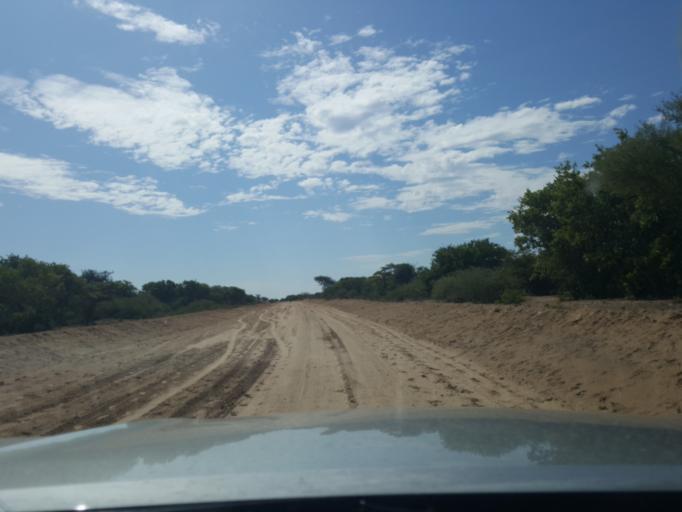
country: BW
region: Kweneng
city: Khudumelapye
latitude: -23.8636
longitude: 24.8883
